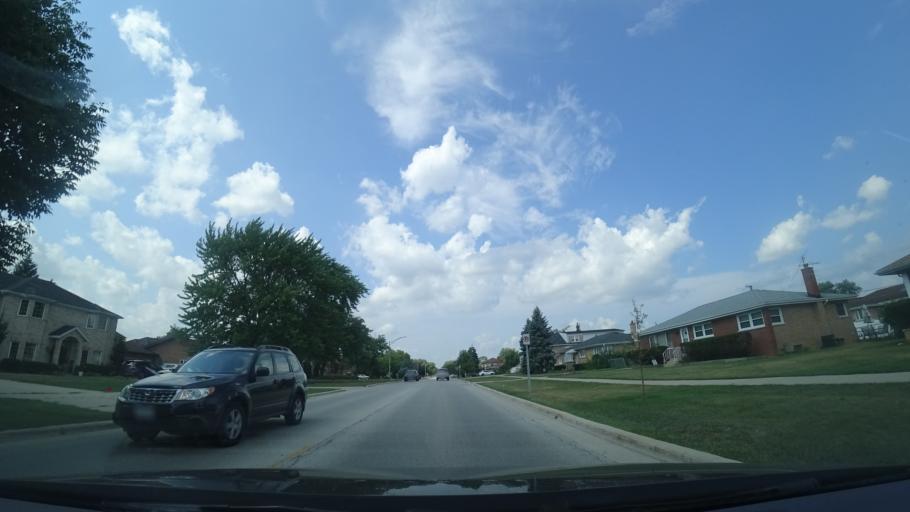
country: US
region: Illinois
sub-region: Cook County
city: Norridge
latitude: 41.9679
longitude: -87.8267
